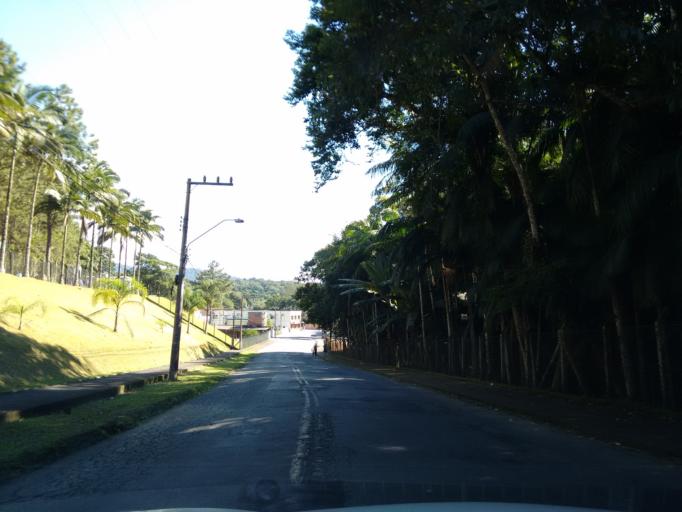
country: BR
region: Santa Catarina
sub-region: Blumenau
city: Blumenau
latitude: -26.8851
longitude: -49.1373
